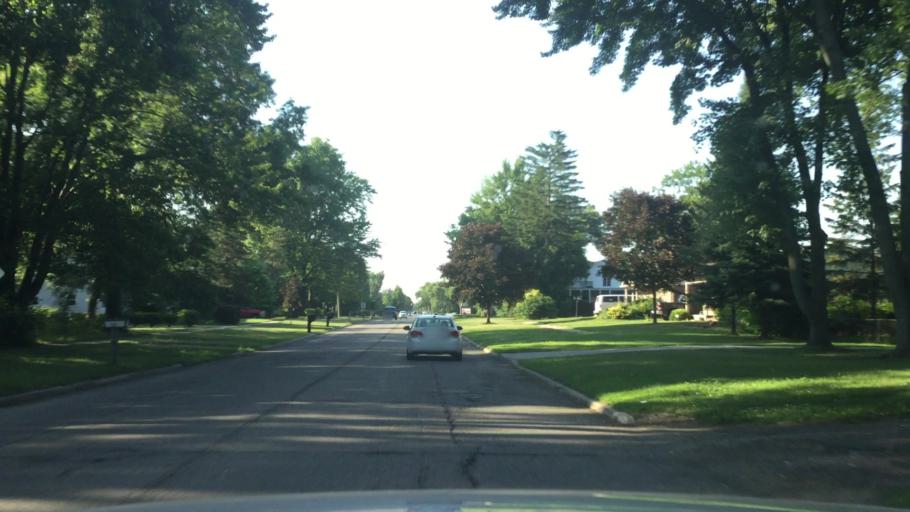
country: US
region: Michigan
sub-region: Wayne County
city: Westland
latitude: 42.3195
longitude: -83.3792
